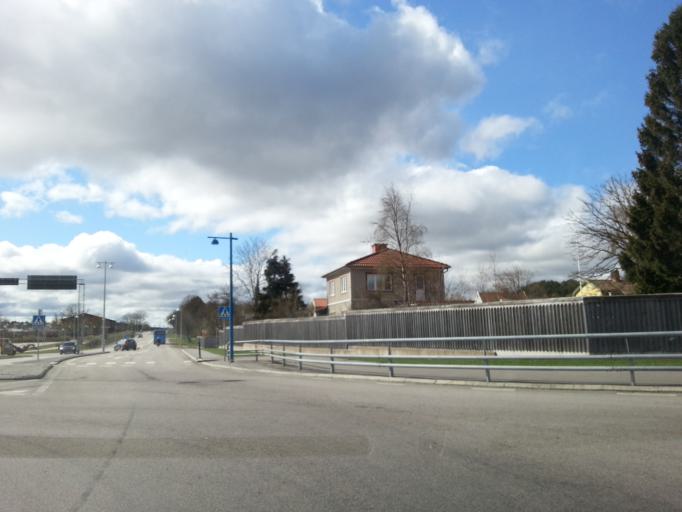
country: SE
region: Vaestra Goetaland
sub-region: Kungalvs Kommun
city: Kungalv
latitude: 57.8653
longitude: 11.9250
